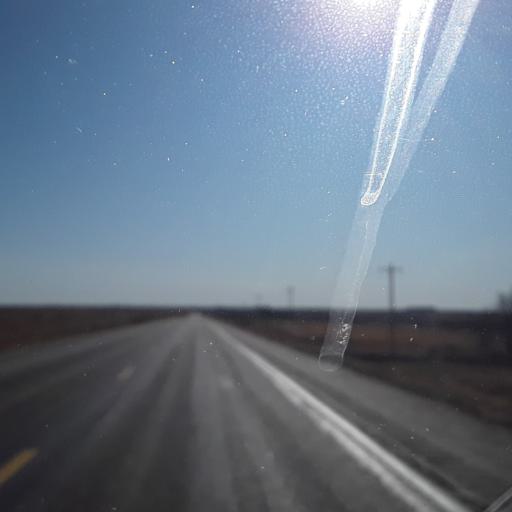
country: US
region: Nebraska
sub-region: Frontier County
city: Stockville
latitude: 40.5300
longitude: -100.6490
